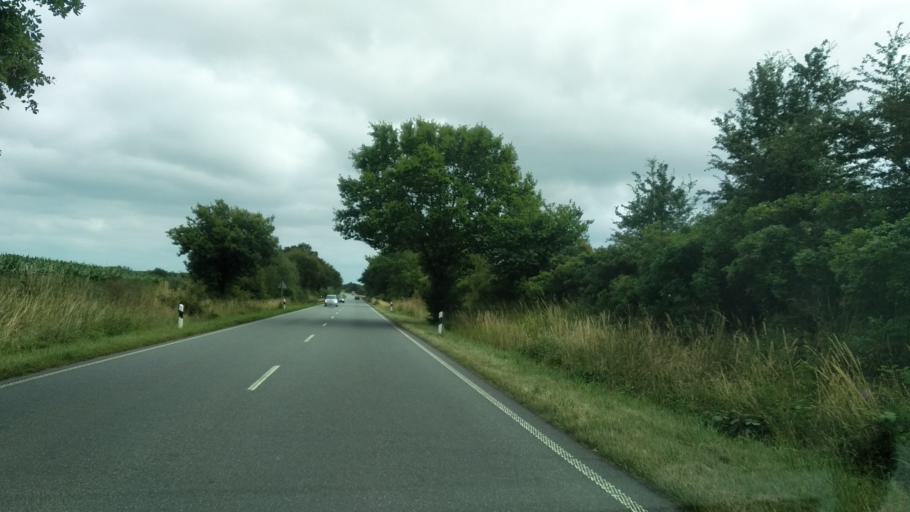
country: DE
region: Schleswig-Holstein
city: Neuberend
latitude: 54.5445
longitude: 9.5471
